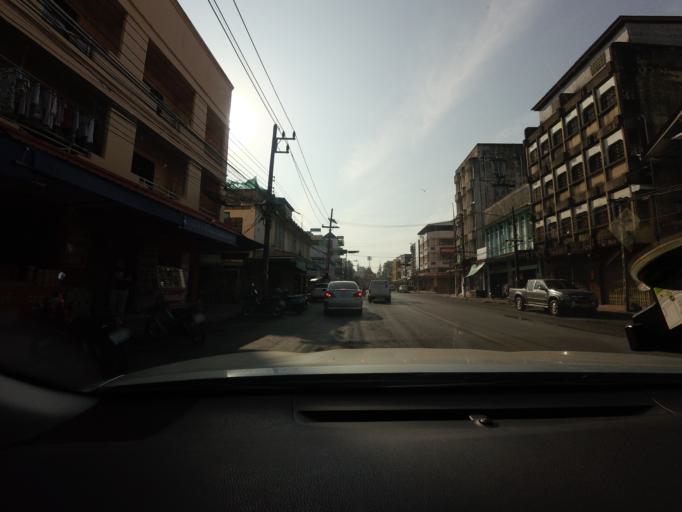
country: TH
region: Yala
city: Yala
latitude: 6.5576
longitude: 101.2893
